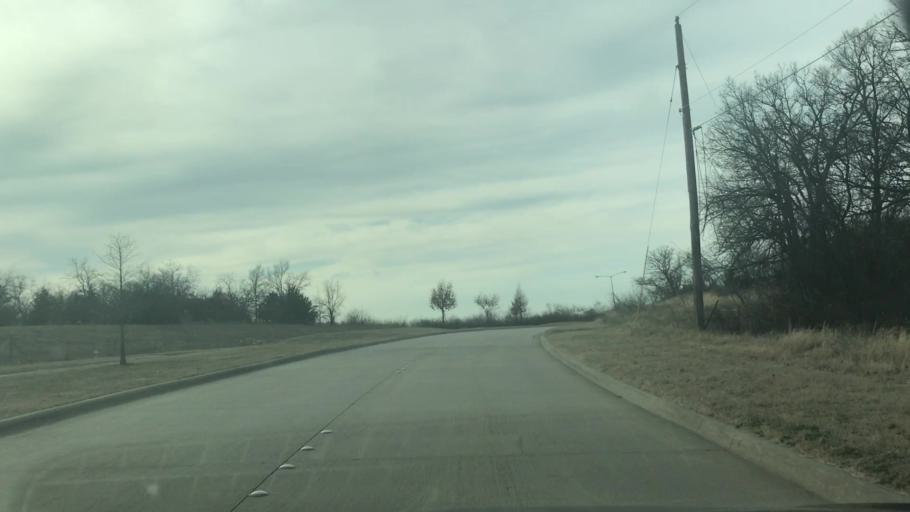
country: US
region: Texas
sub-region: Dallas County
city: Coppell
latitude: 32.9975
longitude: -97.0203
